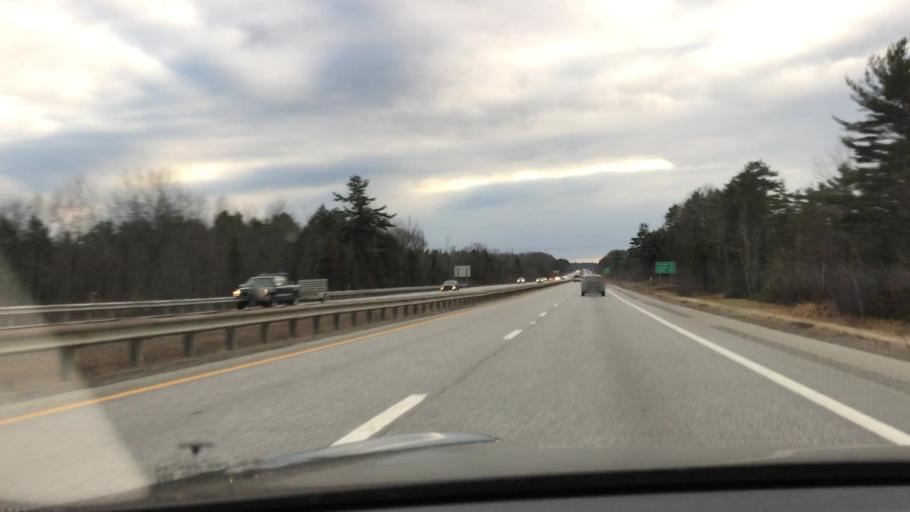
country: US
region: Maine
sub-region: Kennebec County
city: Hallowell
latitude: 44.2595
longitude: -69.8071
